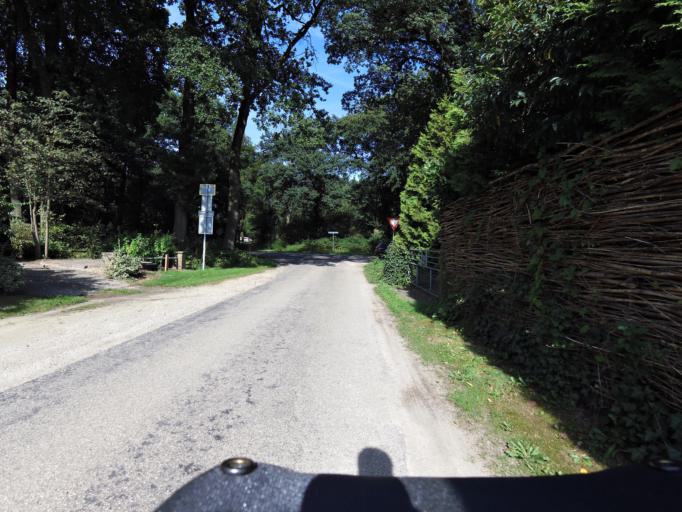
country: NL
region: Gelderland
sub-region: Gemeente Apeldoorn
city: Uddel
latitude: 52.2205
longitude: 5.7702
